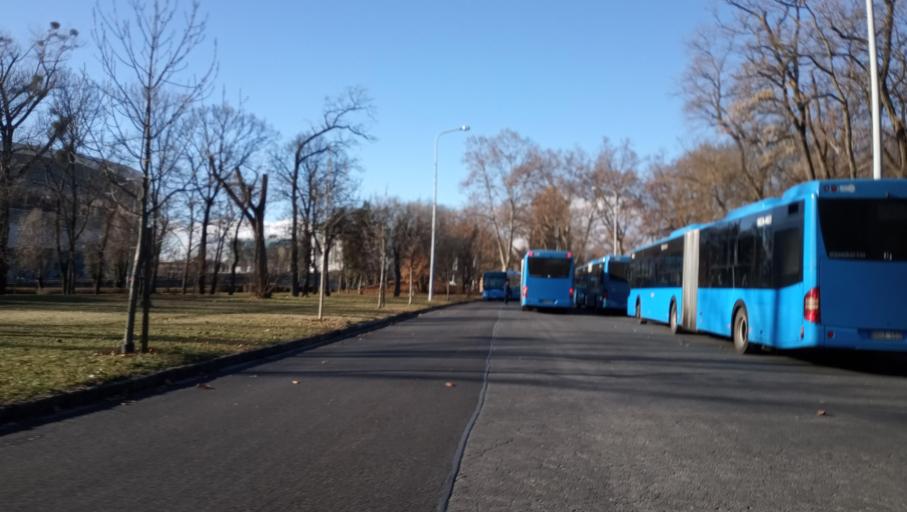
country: HU
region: Budapest
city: Budapest VIII. keruelet
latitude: 47.4750
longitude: 19.1033
